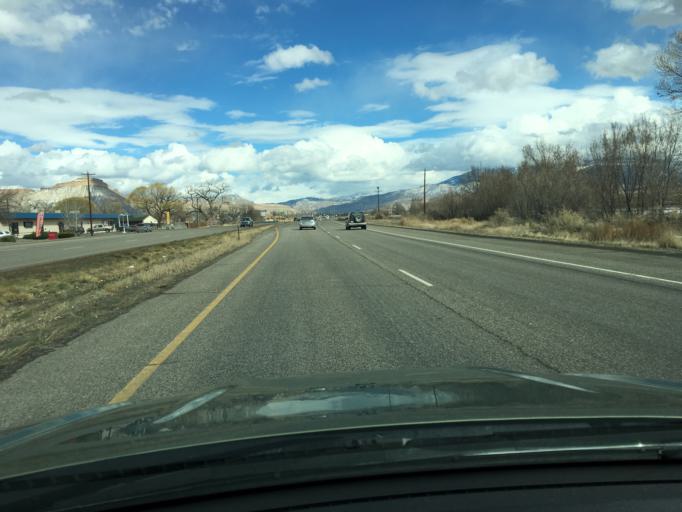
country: US
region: Colorado
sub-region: Mesa County
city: Fruitvale
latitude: 39.0811
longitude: -108.4803
